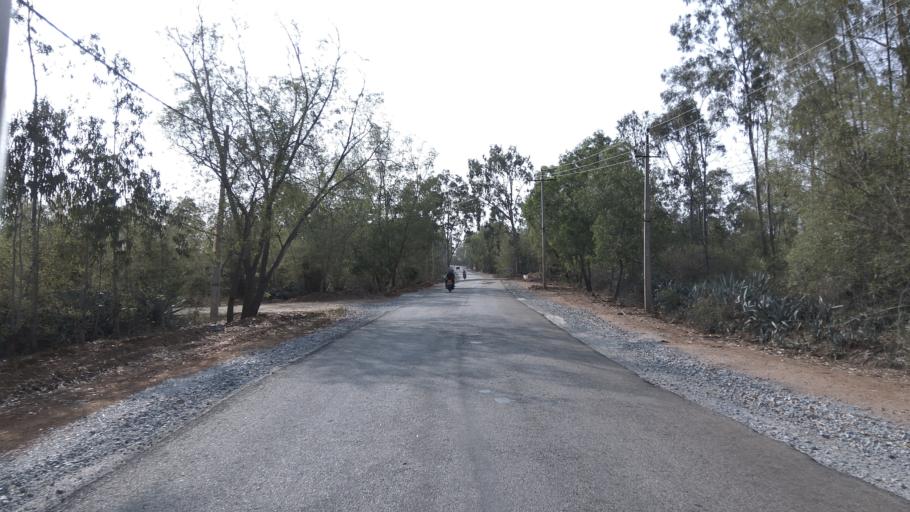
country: IN
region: Karnataka
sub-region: Kolar
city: Kolar
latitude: 13.0861
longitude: 78.2163
